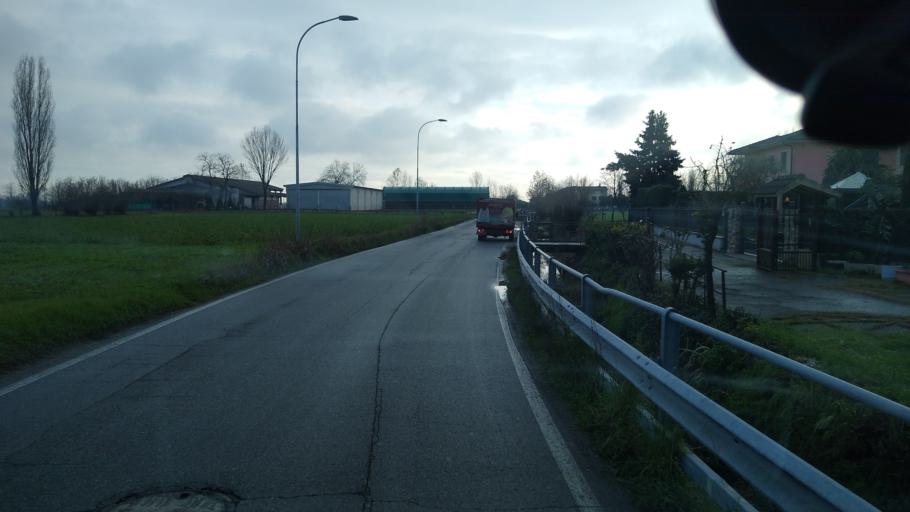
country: IT
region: Lombardy
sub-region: Provincia di Bergamo
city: Misano di Gera d'Adda
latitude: 45.4686
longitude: 9.6257
